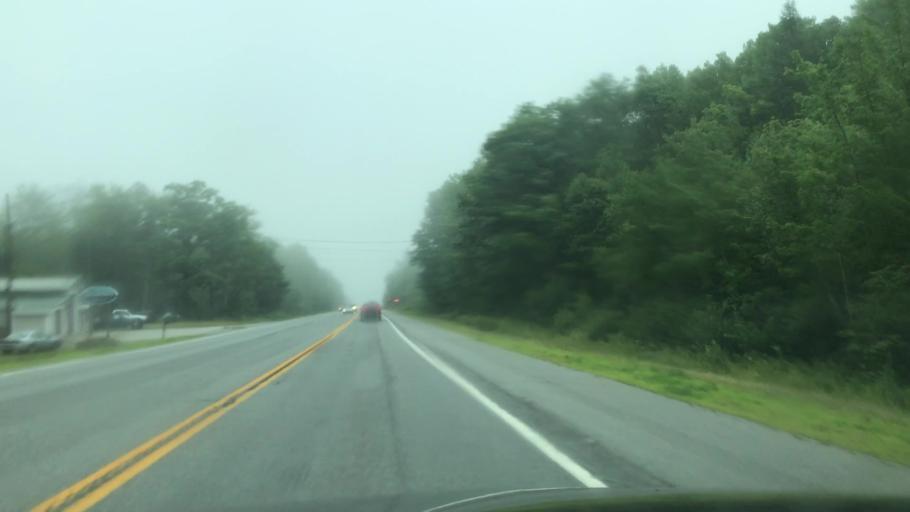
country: US
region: Maine
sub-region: Lincoln County
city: Waldoboro
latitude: 44.0989
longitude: -69.4041
